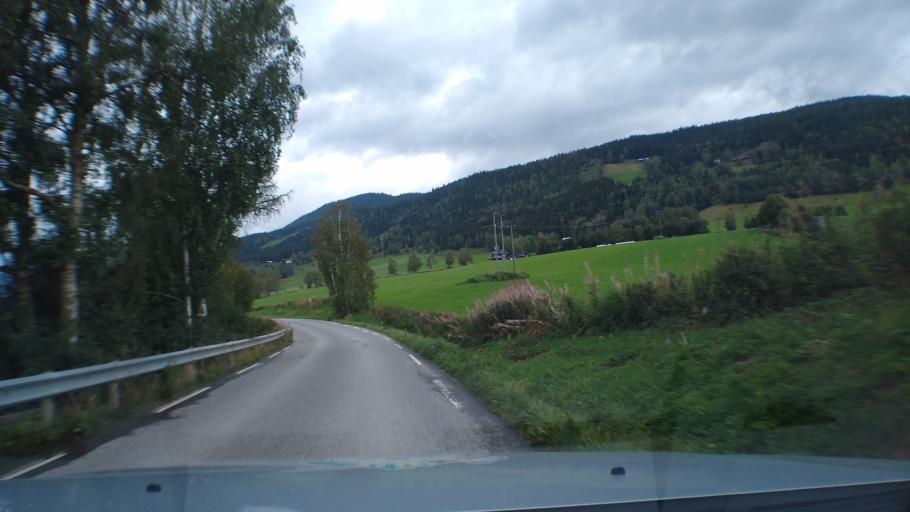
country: NO
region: Oppland
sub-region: Ringebu
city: Ringebu
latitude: 61.5438
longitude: 10.1160
